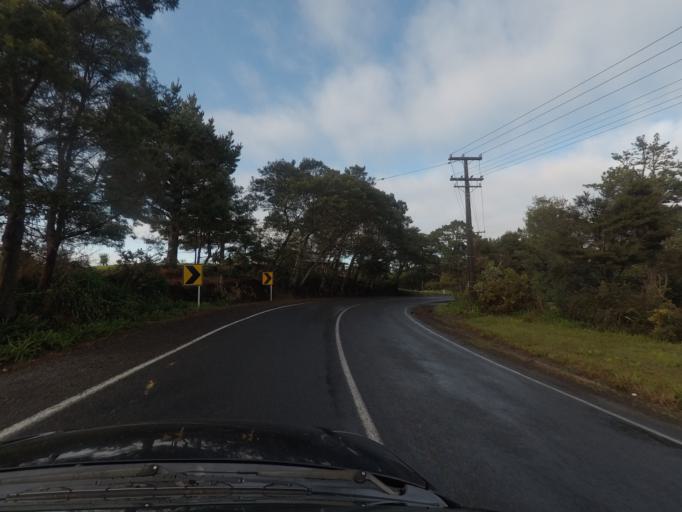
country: NZ
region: Auckland
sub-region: Auckland
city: Waitakere
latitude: -36.9097
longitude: 174.6092
